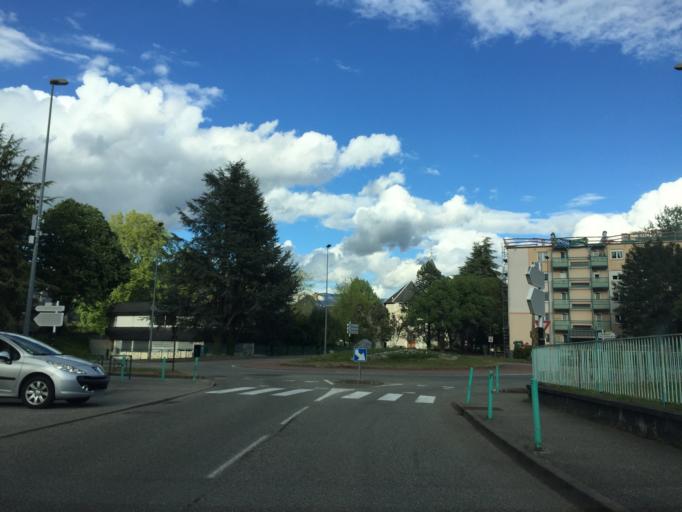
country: FR
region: Rhone-Alpes
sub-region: Departement de la Savoie
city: Cognin
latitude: 45.5623
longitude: 5.8932
